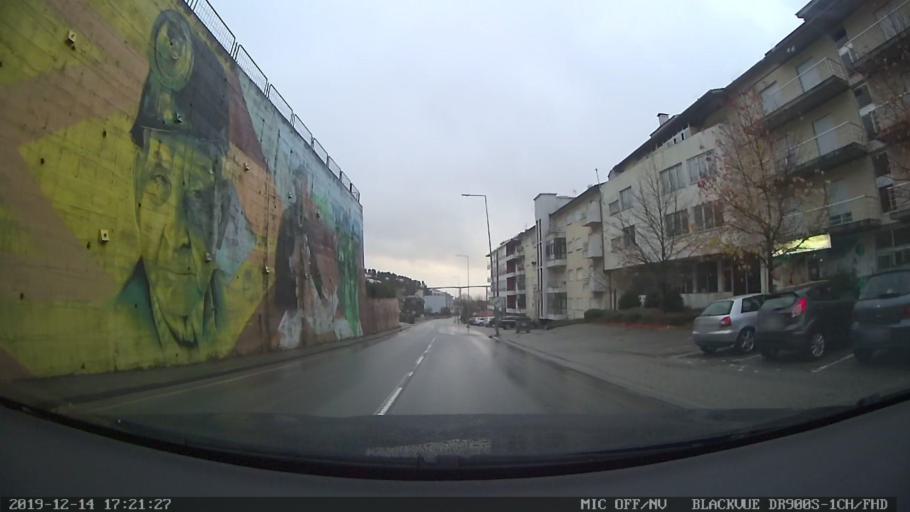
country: PT
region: Vila Real
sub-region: Vila Pouca de Aguiar
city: Vila Pouca de Aguiar
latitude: 41.4979
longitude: -7.6416
